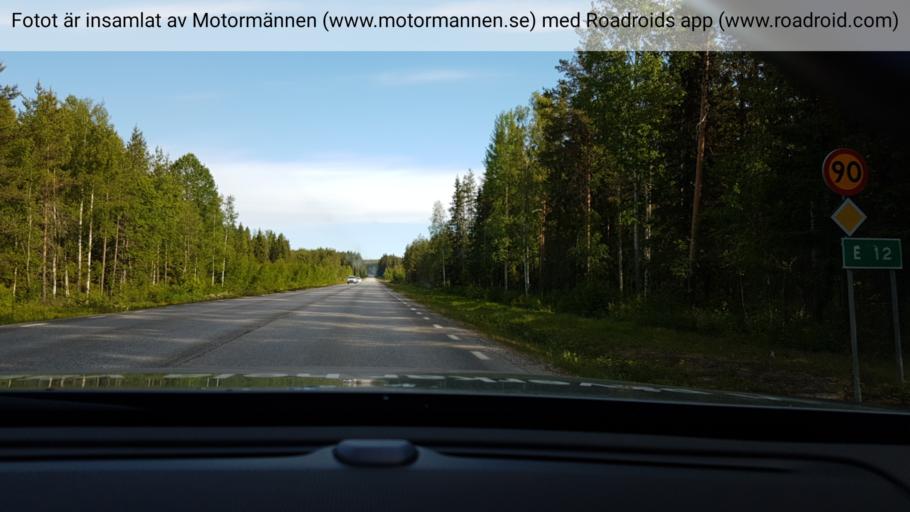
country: SE
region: Vaesterbotten
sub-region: Vannas Kommun
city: Vaennaes
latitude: 63.9488
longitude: 19.7586
